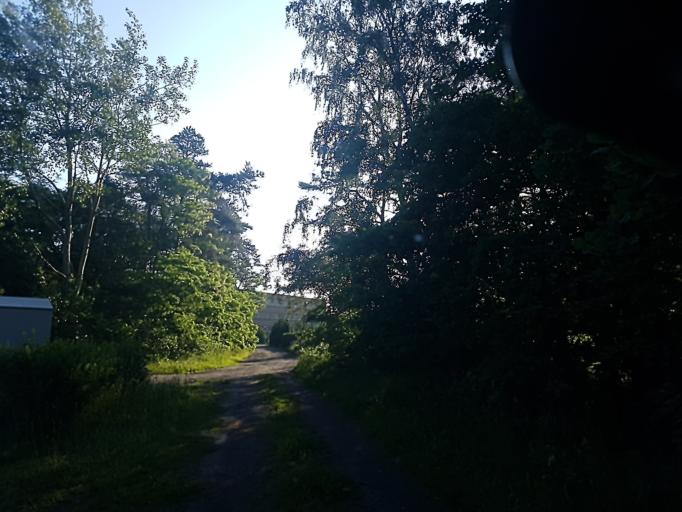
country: DE
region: Brandenburg
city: Schonborn
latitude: 51.6004
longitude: 13.4761
